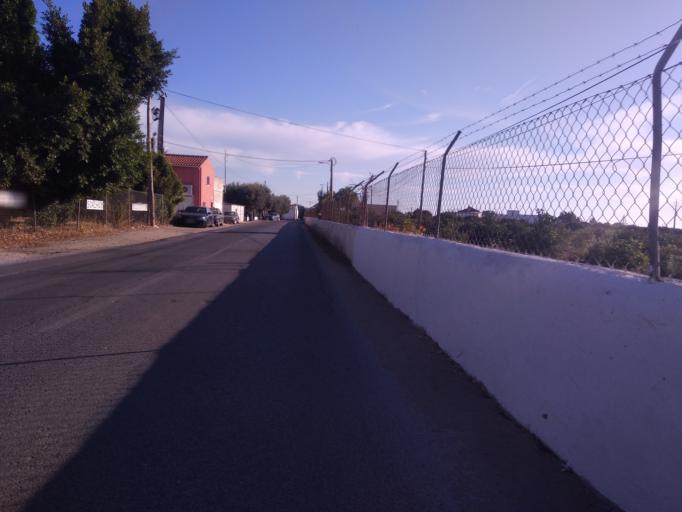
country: PT
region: Faro
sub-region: Faro
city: Faro
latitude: 37.0475
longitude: -7.9377
